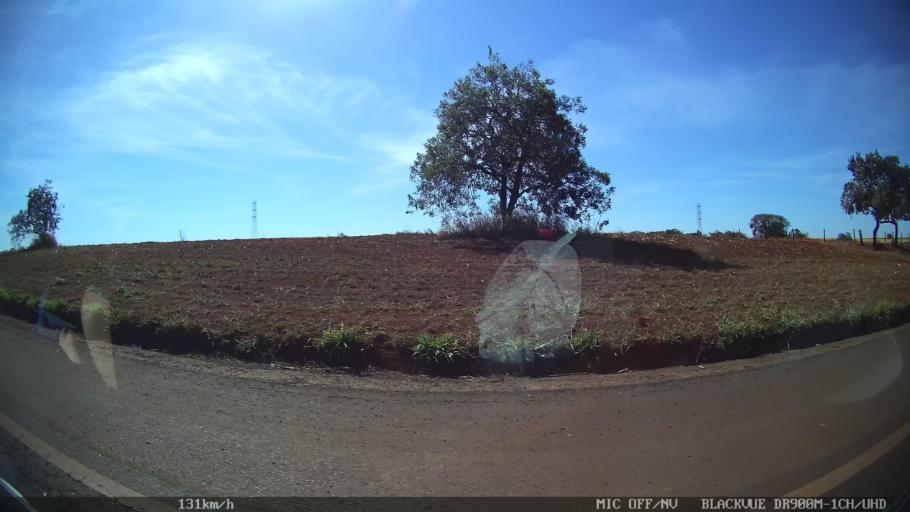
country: BR
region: Sao Paulo
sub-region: Ipua
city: Ipua
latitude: -20.4528
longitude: -48.1686
